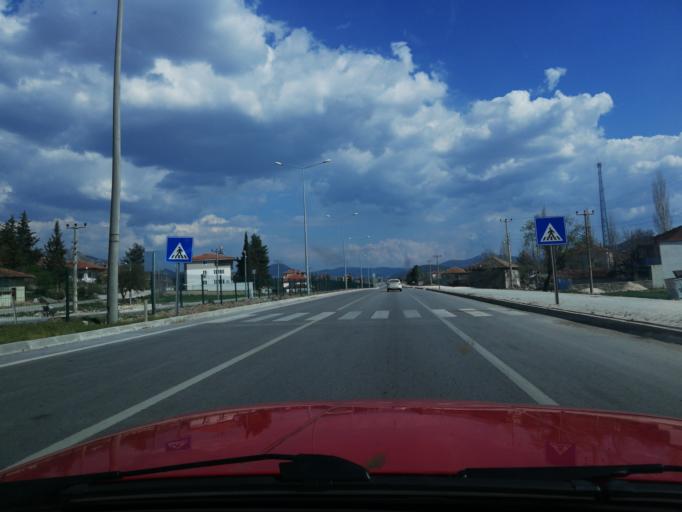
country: TR
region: Burdur
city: Celtikci
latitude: 37.5318
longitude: 30.4877
